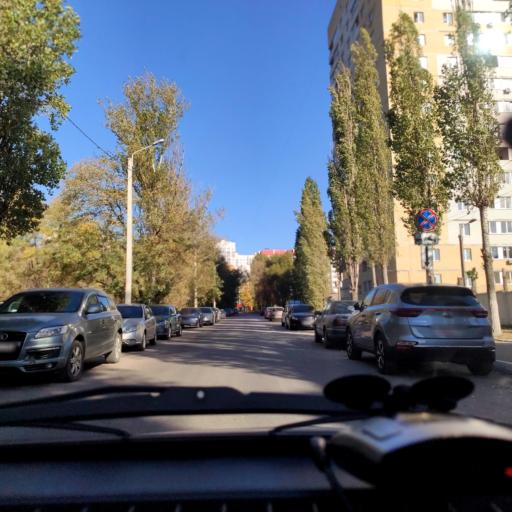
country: RU
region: Voronezj
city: Voronezh
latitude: 51.6901
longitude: 39.1444
